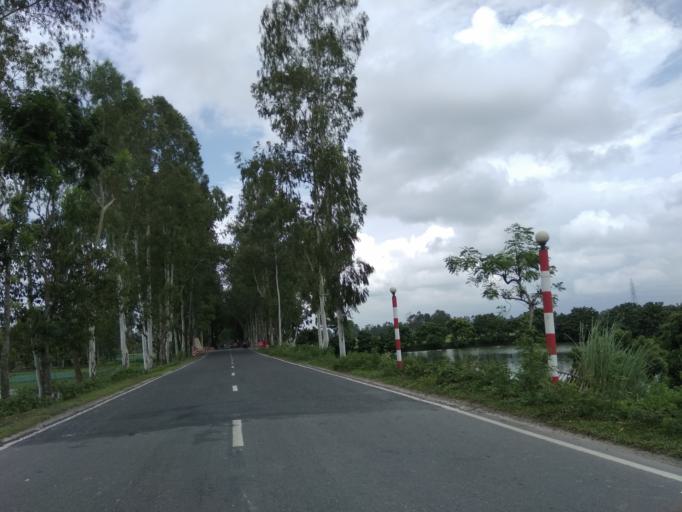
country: BD
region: Rajshahi
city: Saidpur
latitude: 25.7690
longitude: 88.8122
